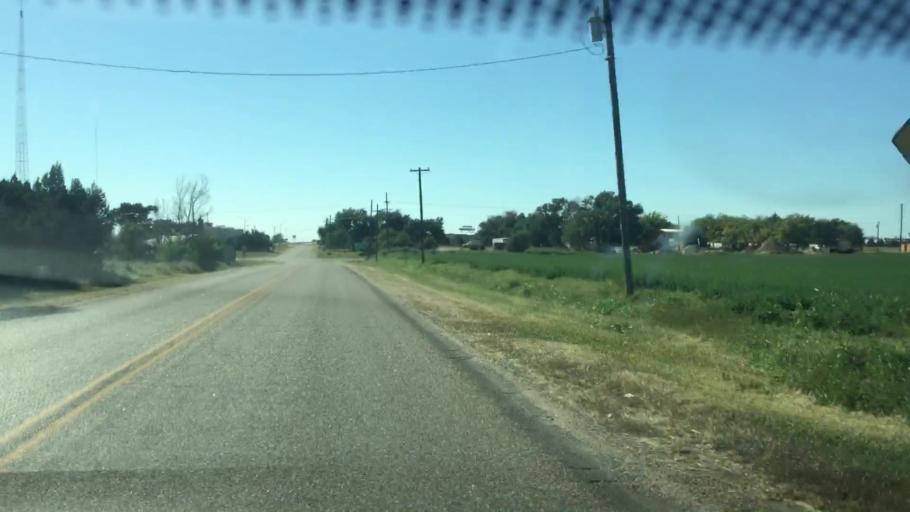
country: US
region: Colorado
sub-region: Prowers County
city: Lamar
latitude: 38.1167
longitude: -102.6161
